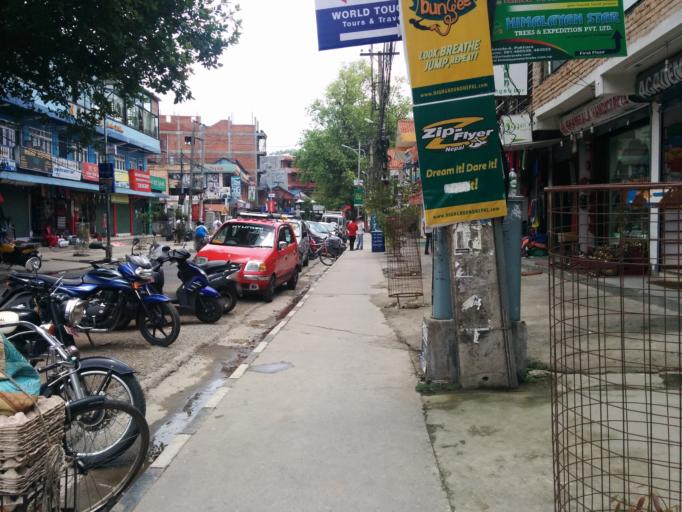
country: NP
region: Western Region
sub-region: Gandaki Zone
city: Pokhara
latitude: 28.2093
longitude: 83.9571
